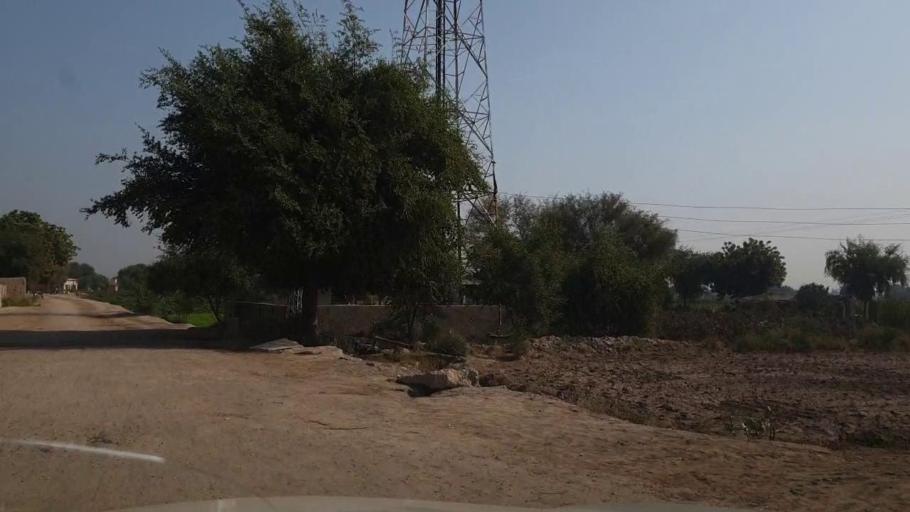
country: PK
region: Sindh
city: Bhan
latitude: 26.5275
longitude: 67.7787
